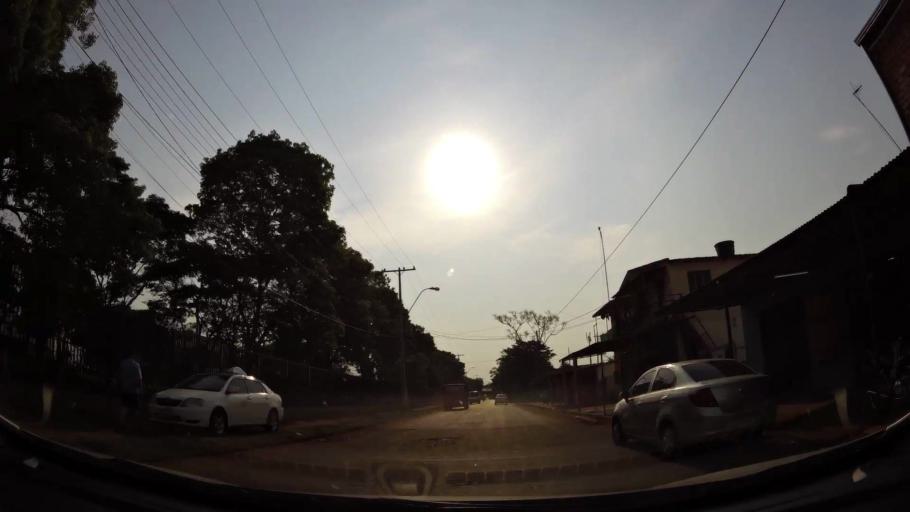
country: PY
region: Alto Parana
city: Ciudad del Este
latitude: -25.4830
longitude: -54.6719
